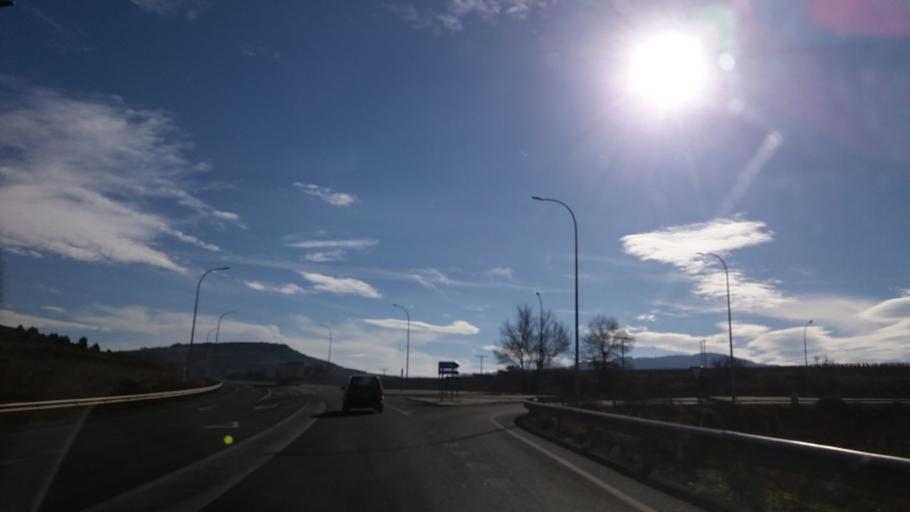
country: ES
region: La Rioja
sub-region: Provincia de La Rioja
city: Cenicero
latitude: 42.4720
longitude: -2.6410
